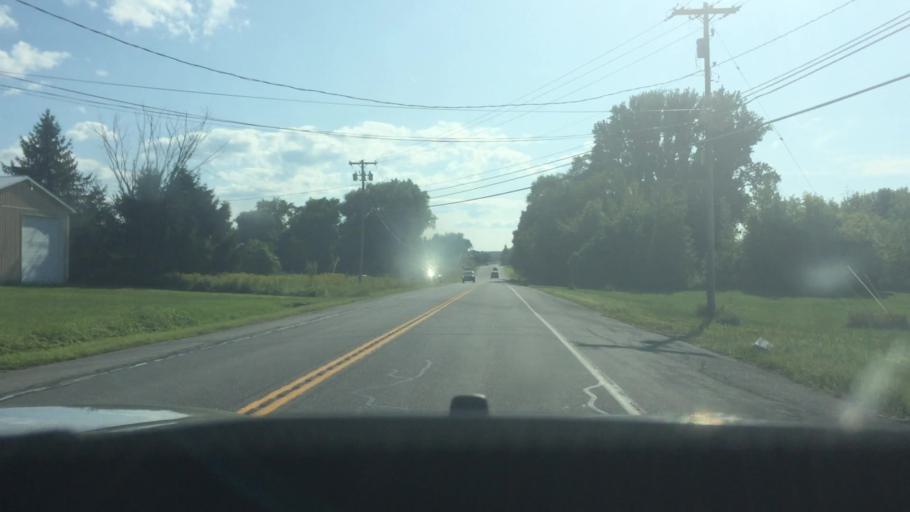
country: US
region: New York
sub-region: Franklin County
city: Malone
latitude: 44.8353
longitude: -74.3221
